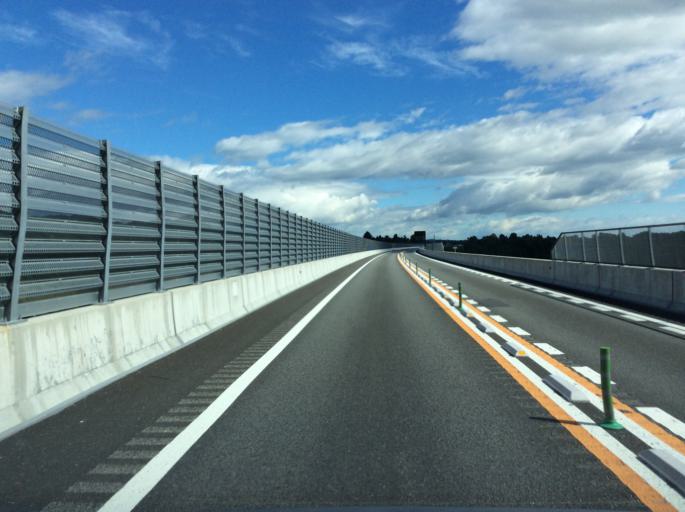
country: JP
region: Fukushima
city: Namie
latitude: 37.5952
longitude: 140.9270
